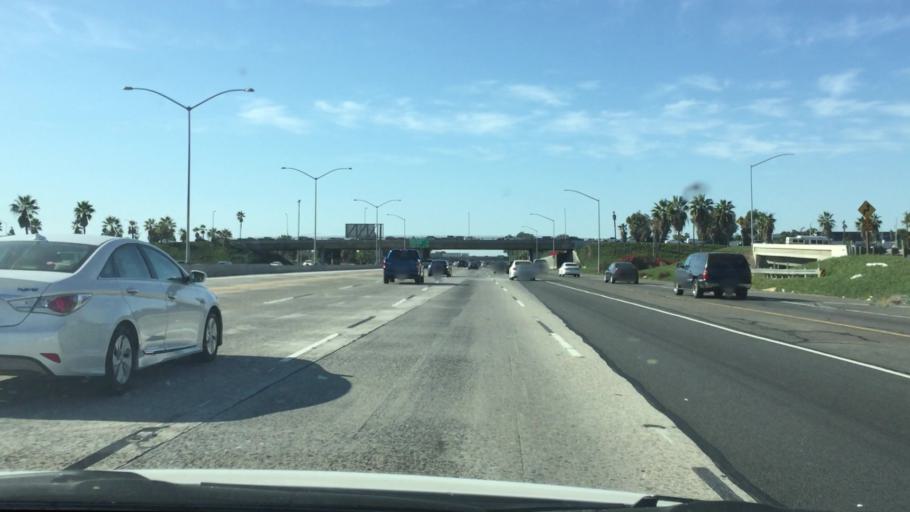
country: US
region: California
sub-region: Orange County
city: Costa Mesa
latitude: 33.6876
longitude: -117.8827
